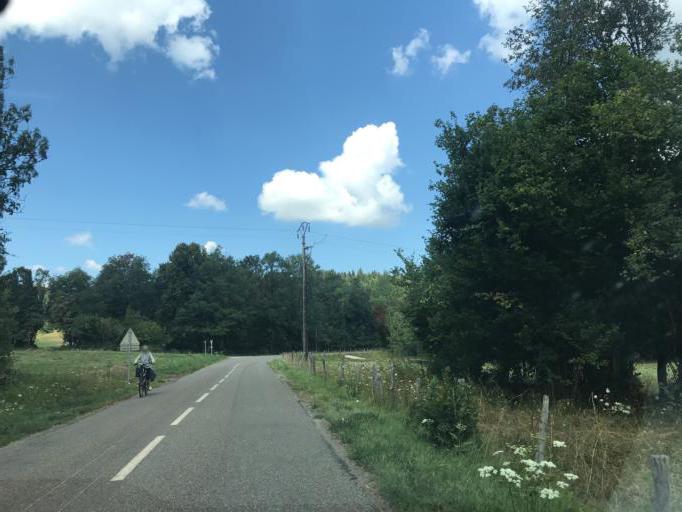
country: FR
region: Franche-Comte
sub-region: Departement du Jura
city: Clairvaux-les-Lacs
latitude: 46.5116
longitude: 5.7895
